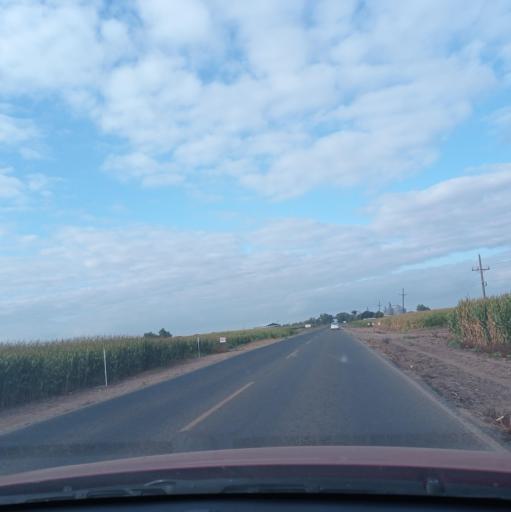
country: MX
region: Sinaloa
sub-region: Guasave
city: Las Quemazones
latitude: 25.6600
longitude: -108.5222
